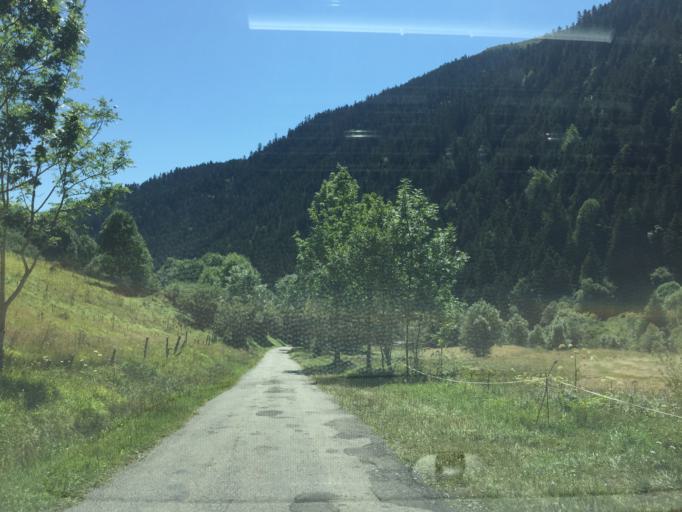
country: FR
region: Midi-Pyrenees
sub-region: Departement des Hautes-Pyrenees
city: Saint-Lary-Soulan
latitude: 42.8515
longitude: 0.2733
